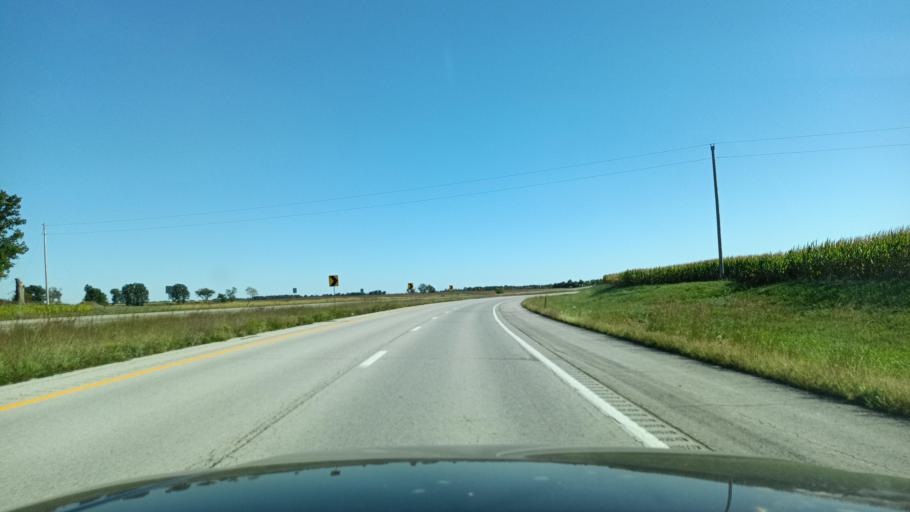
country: US
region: Missouri
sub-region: Randolph County
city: Moberly
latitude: 39.3154
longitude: -92.3737
